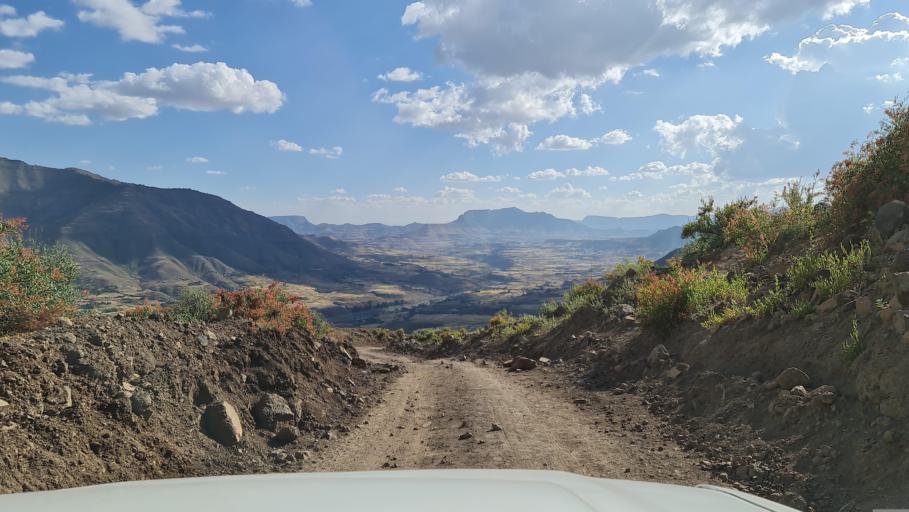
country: ET
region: Amhara
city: Debark'
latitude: 13.1220
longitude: 38.0208
